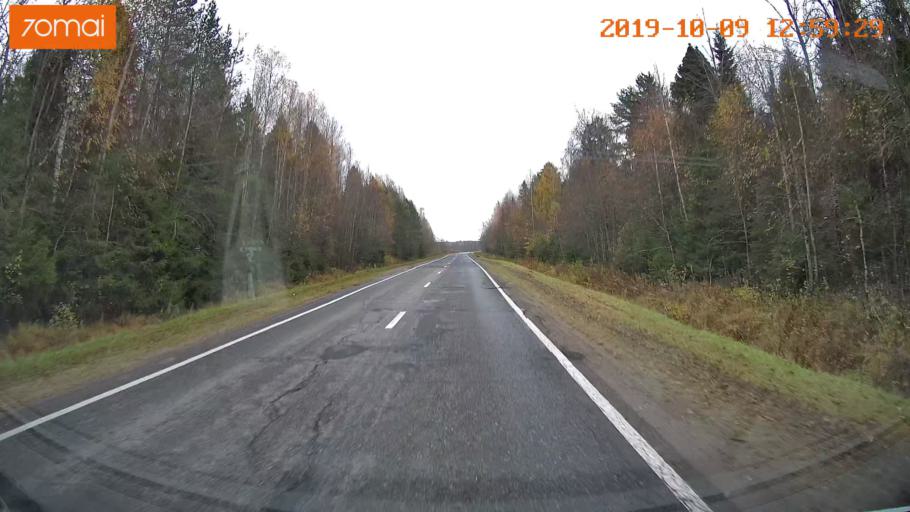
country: RU
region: Jaroslavl
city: Prechistoye
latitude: 58.3833
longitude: 40.4653
